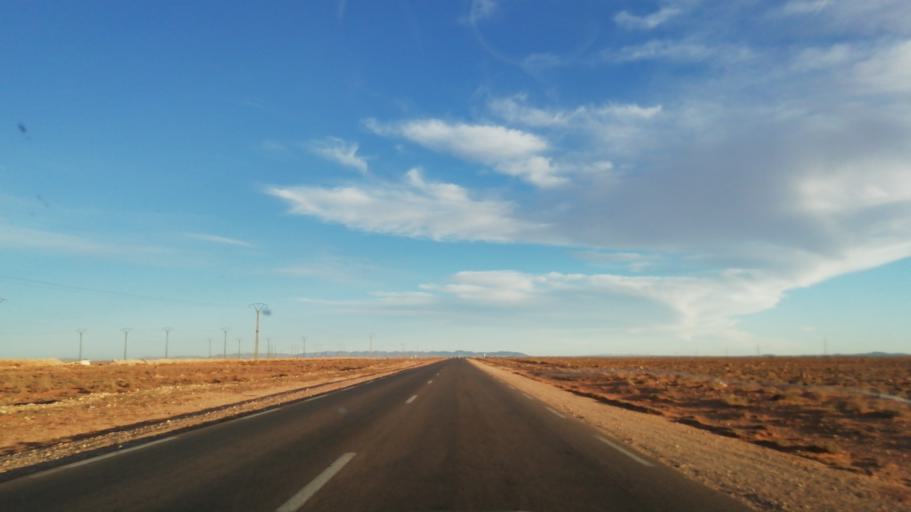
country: DZ
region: Wilaya de Naama
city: Naama
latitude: 33.7370
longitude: -0.7652
